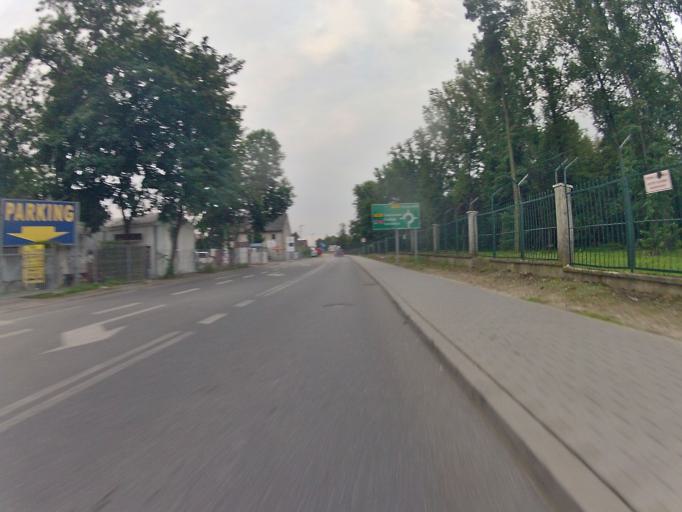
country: PL
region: Lesser Poland Voivodeship
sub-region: Powiat krakowski
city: Balice
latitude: 50.0706
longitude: 19.8000
